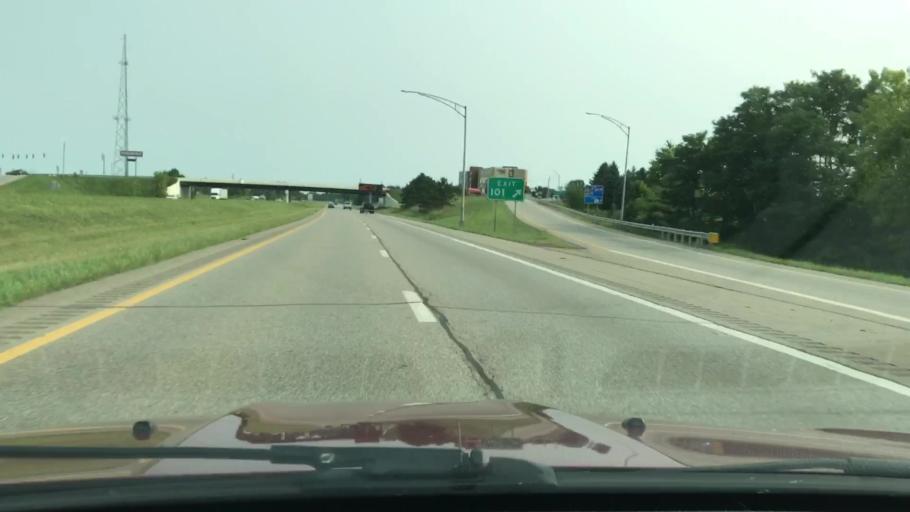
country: US
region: Ohio
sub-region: Stark County
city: Canton
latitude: 40.7485
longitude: -81.4062
